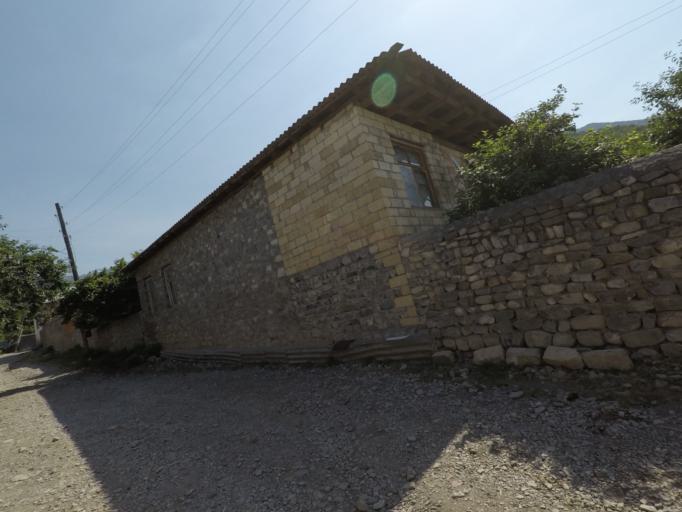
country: AZ
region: Qakh Rayon
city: Cinarli
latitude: 41.4847
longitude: 46.8501
